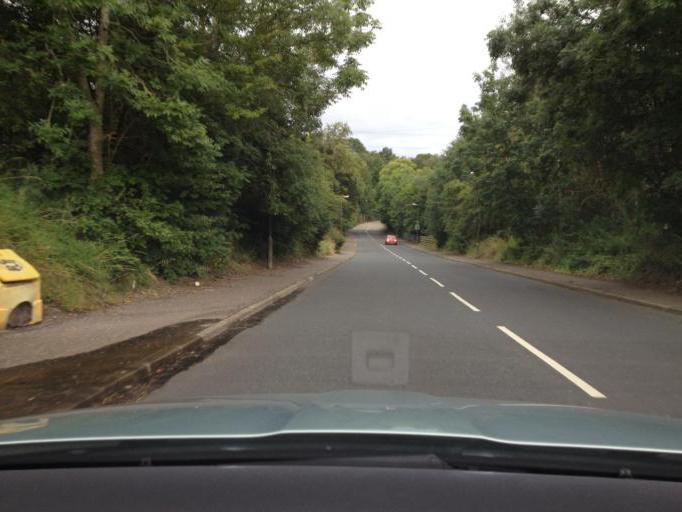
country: GB
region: Scotland
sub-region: West Lothian
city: Armadale
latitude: 55.9324
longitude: -3.6993
